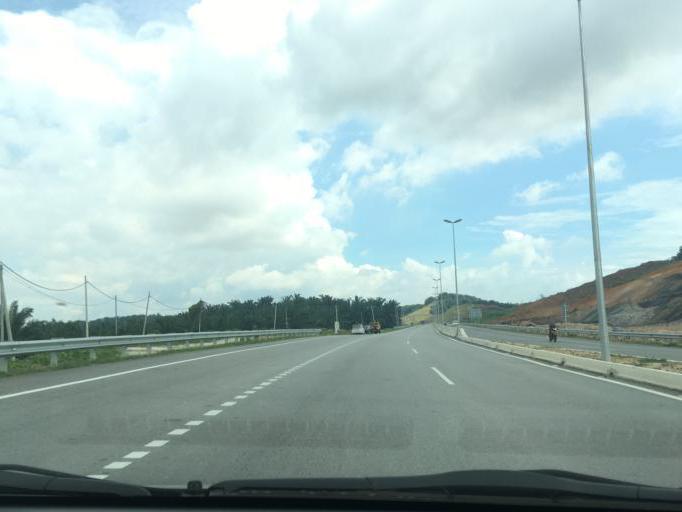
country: MY
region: Selangor
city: Batu Arang
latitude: 3.2949
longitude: 101.4408
